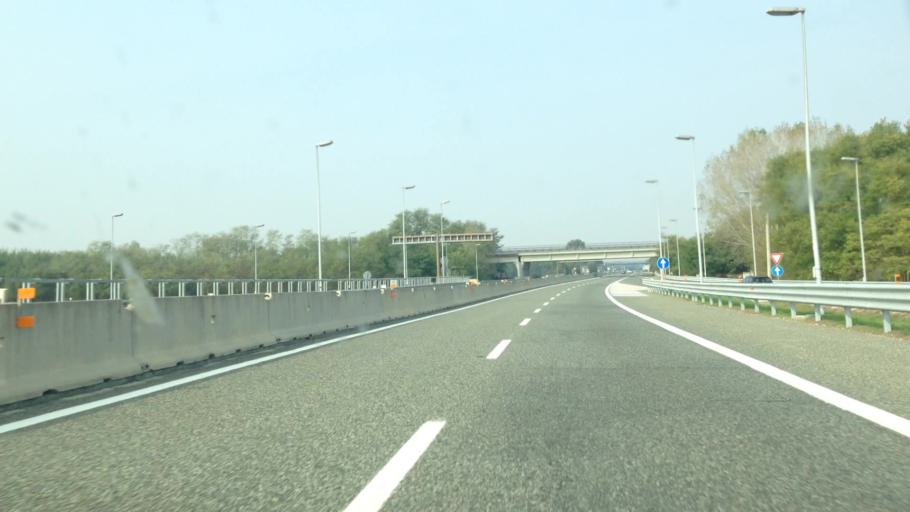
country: IT
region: Piedmont
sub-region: Provincia di Vercelli
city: Stroppiana
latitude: 45.2468
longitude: 8.4628
